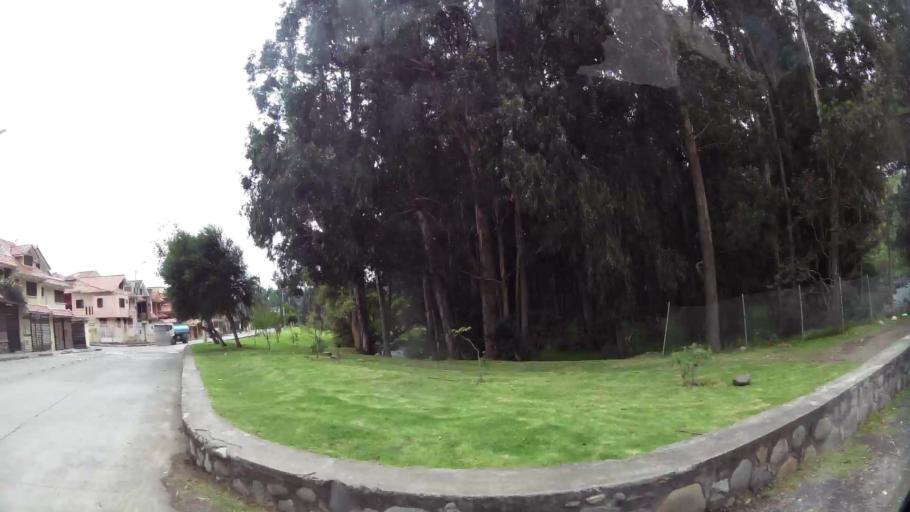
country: EC
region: Azuay
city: Cuenca
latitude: -2.9173
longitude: -79.0132
